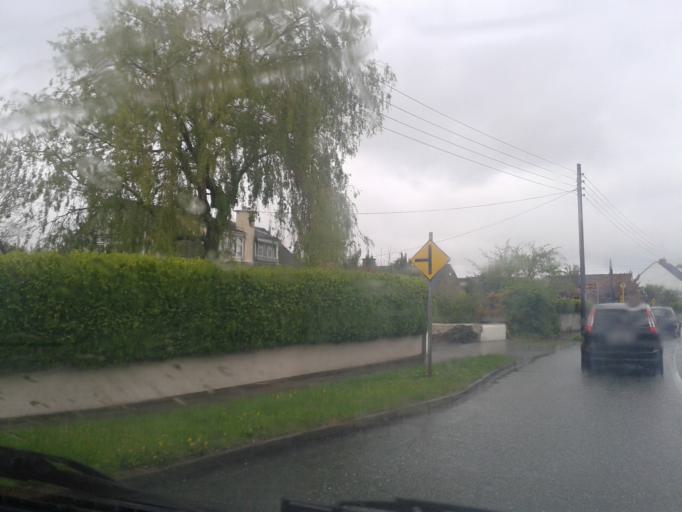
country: IE
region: Leinster
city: Templeogue
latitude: 53.3048
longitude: -6.3223
